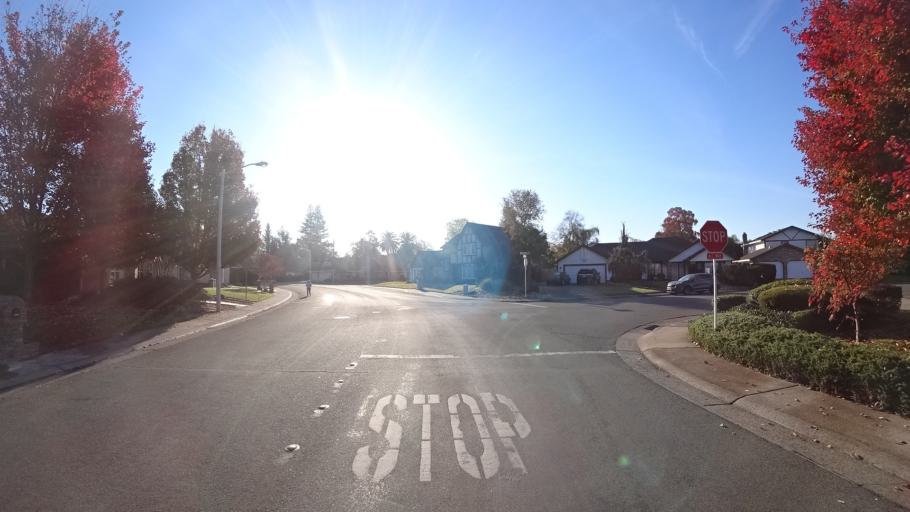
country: US
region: California
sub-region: Sacramento County
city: Citrus Heights
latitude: 38.7230
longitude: -121.2761
